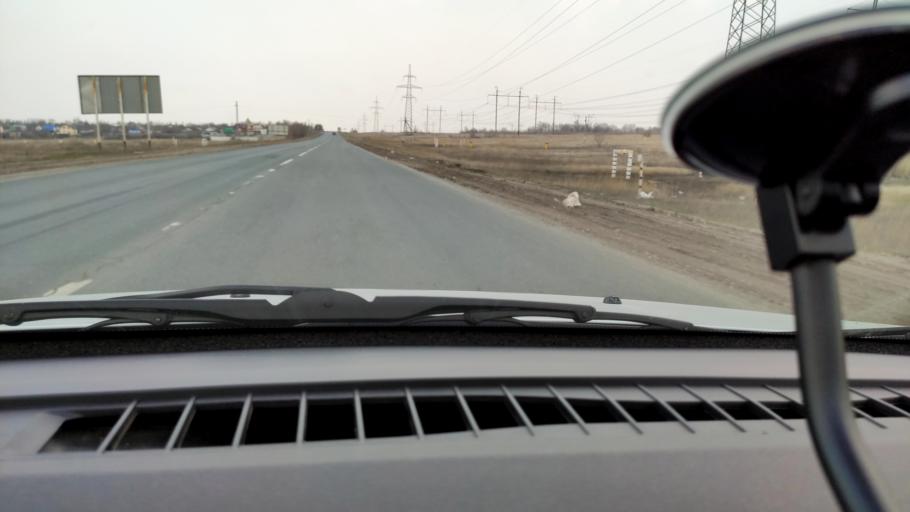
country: RU
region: Samara
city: Dubovyy Umet
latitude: 53.0645
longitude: 50.3777
